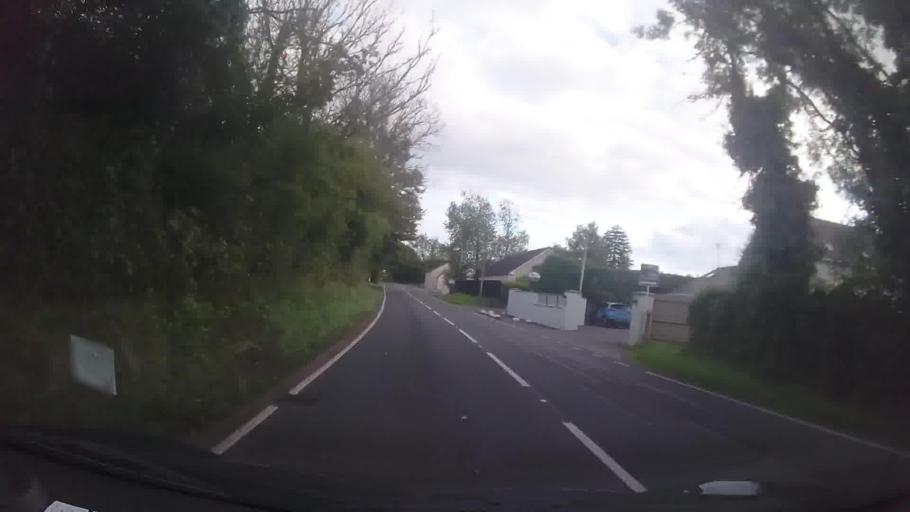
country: GB
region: Wales
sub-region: Pembrokeshire
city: Kilgetty
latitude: 51.7115
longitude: -4.7309
